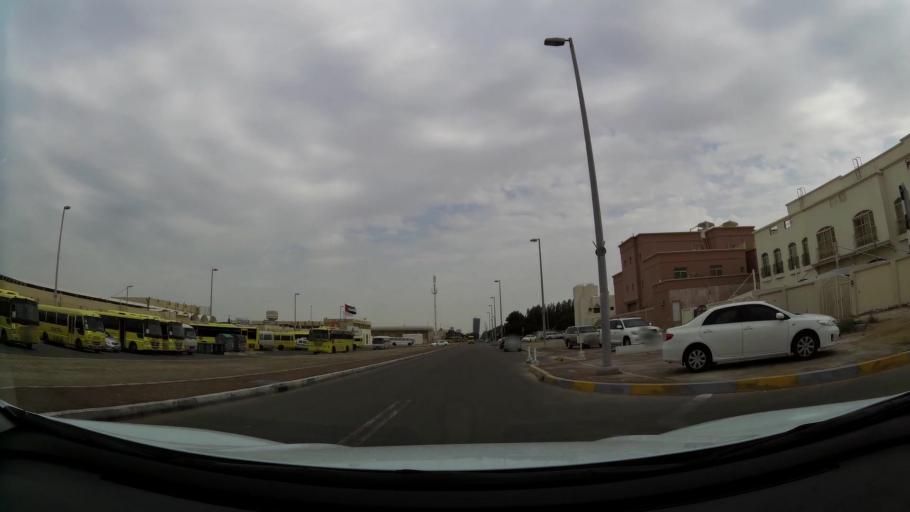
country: AE
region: Abu Dhabi
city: Abu Dhabi
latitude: 24.4308
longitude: 54.4035
